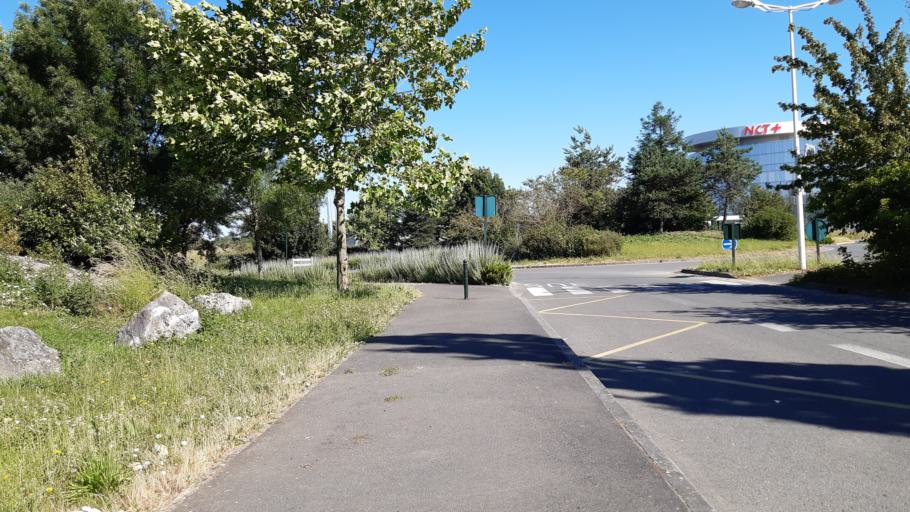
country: FR
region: Centre
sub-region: Departement d'Indre-et-Loire
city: Mettray
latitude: 47.4321
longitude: 0.6667
